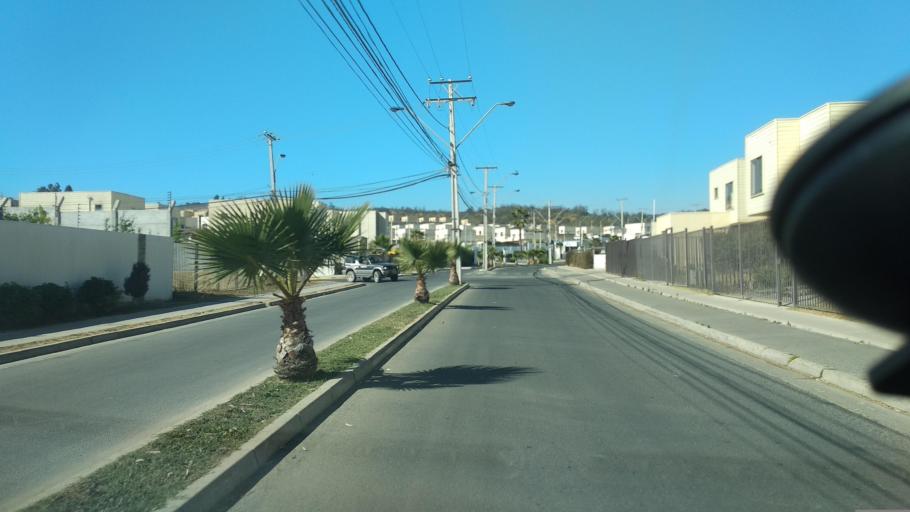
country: CL
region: Valparaiso
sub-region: Provincia de Marga Marga
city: Villa Alemana
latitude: -33.0357
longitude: -71.3879
